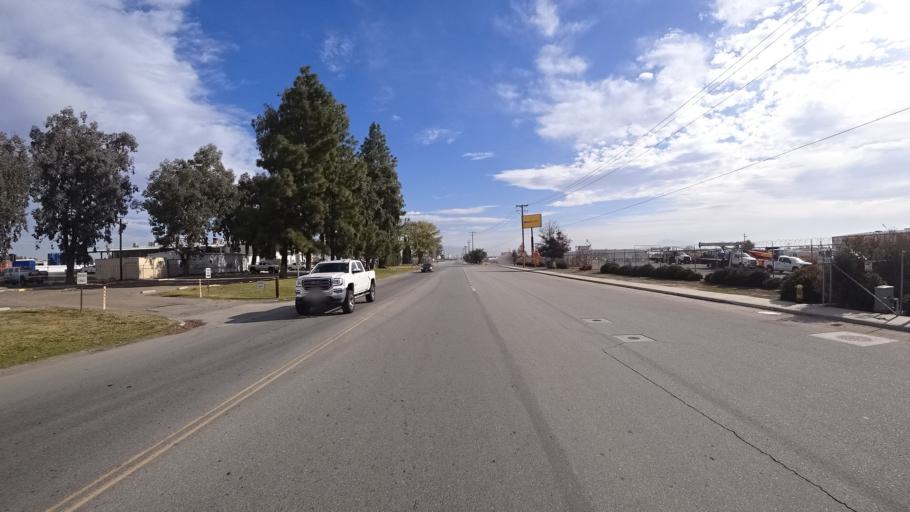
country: US
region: California
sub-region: Kern County
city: Oildale
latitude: 35.4269
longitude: -119.0724
